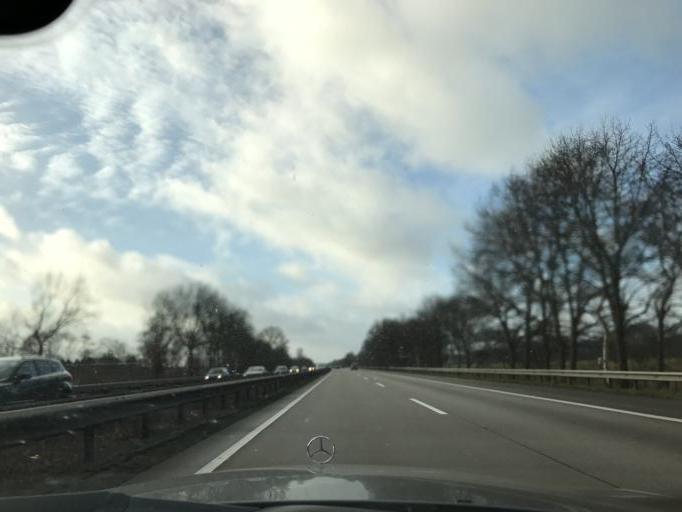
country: DE
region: Lower Saxony
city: Gross Ippener
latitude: 52.9904
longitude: 8.6502
